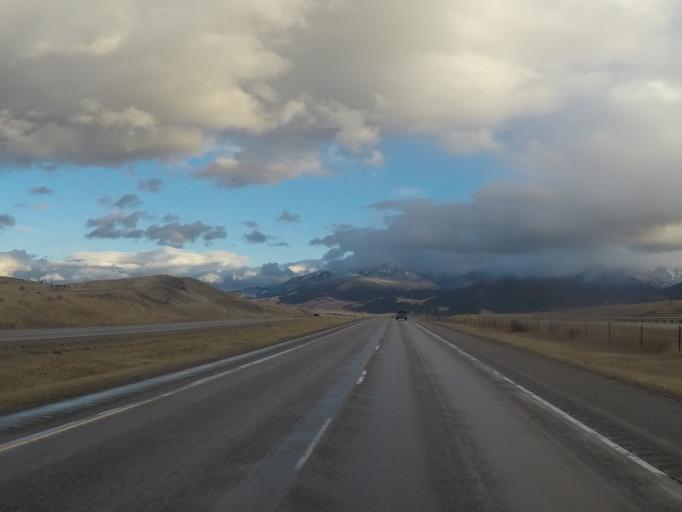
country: US
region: Montana
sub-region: Park County
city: Livingston
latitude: 45.6579
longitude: -110.6319
